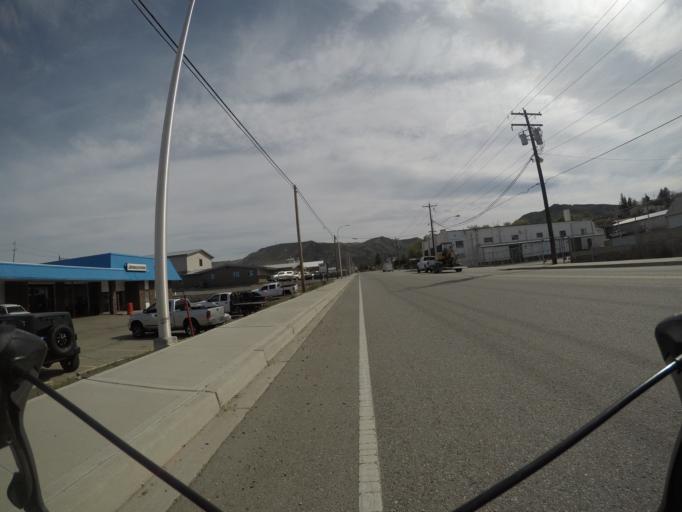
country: US
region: Washington
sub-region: Douglas County
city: East Wenatchee
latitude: 47.4068
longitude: -120.2998
